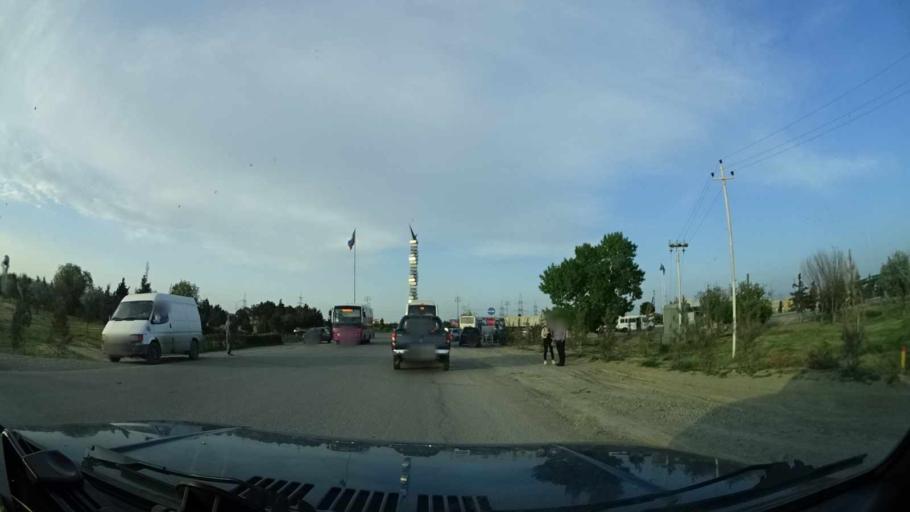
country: AZ
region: Abseron
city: Ceyranbatan
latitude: 40.5681
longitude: 49.6306
